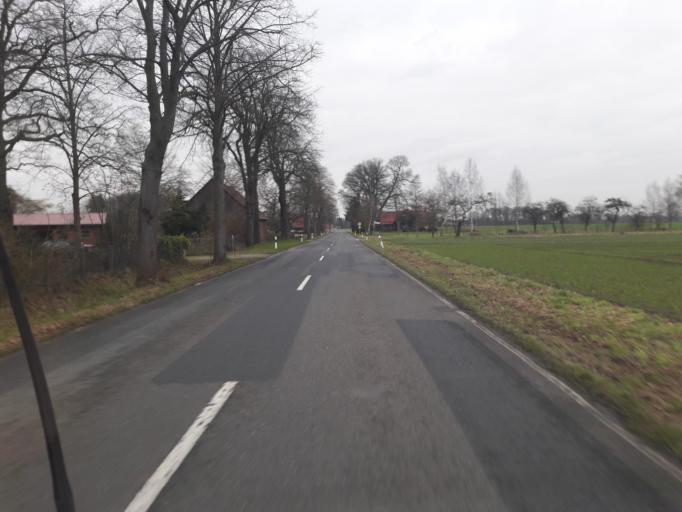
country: DE
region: Lower Saxony
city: Warmsen
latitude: 52.3920
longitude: 8.8552
